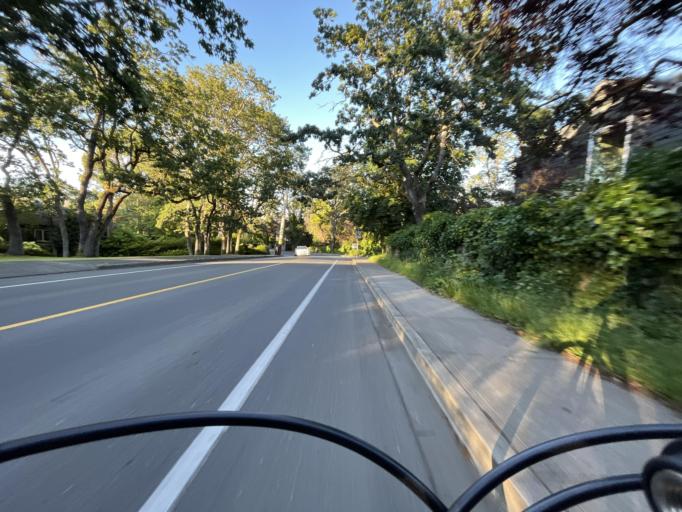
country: CA
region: British Columbia
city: Oak Bay
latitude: 48.4183
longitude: -123.3255
